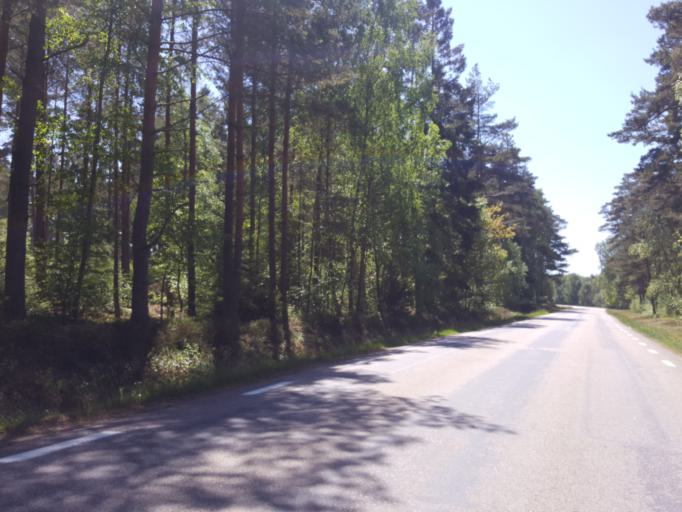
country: SE
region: Halland
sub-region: Laholms Kommun
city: Mellbystrand
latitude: 56.5495
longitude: 12.9688
